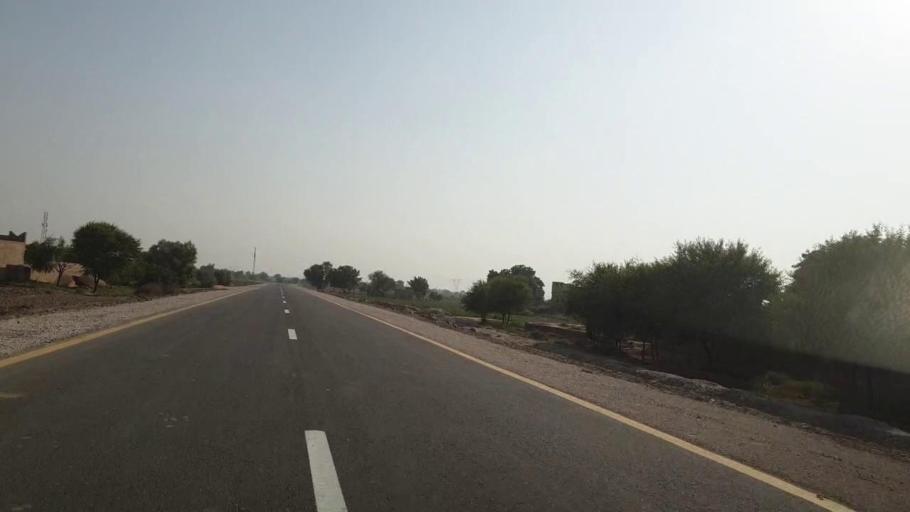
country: PK
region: Sindh
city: Bhan
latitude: 26.4870
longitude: 67.7796
